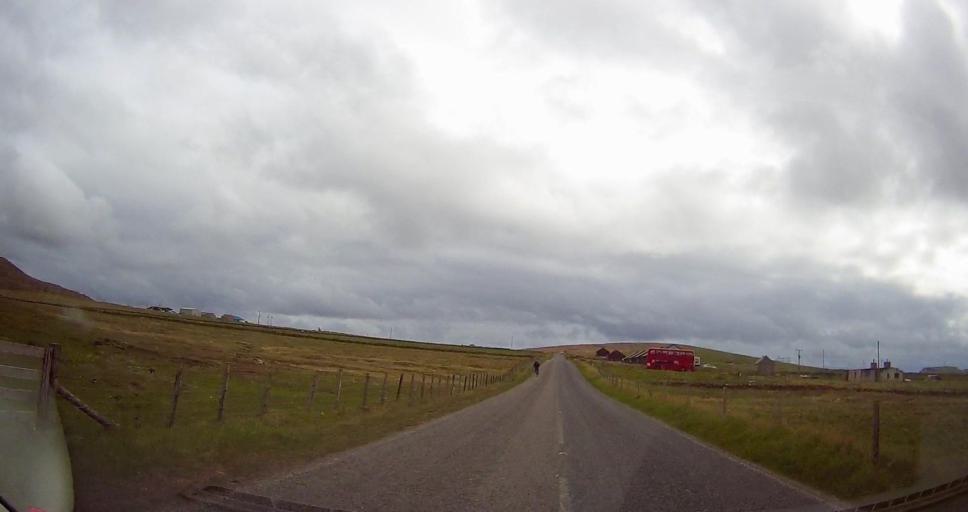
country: GB
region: Scotland
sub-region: Shetland Islands
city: Shetland
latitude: 60.7647
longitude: -0.8436
